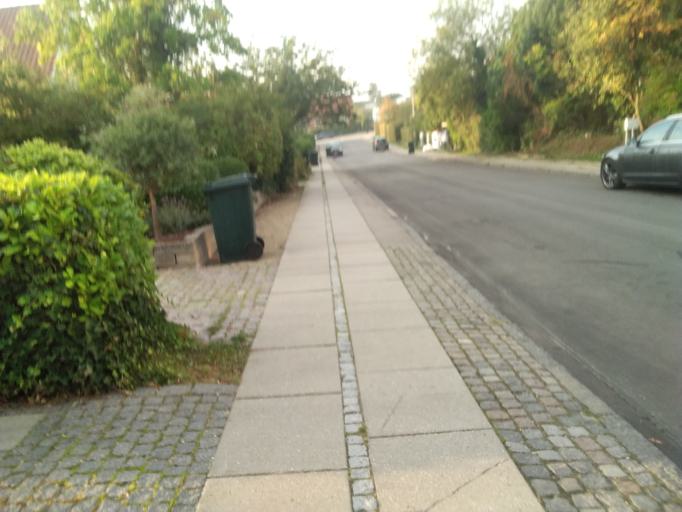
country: DK
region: Capital Region
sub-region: Gladsaxe Municipality
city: Buddinge
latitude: 55.7283
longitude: 12.5091
